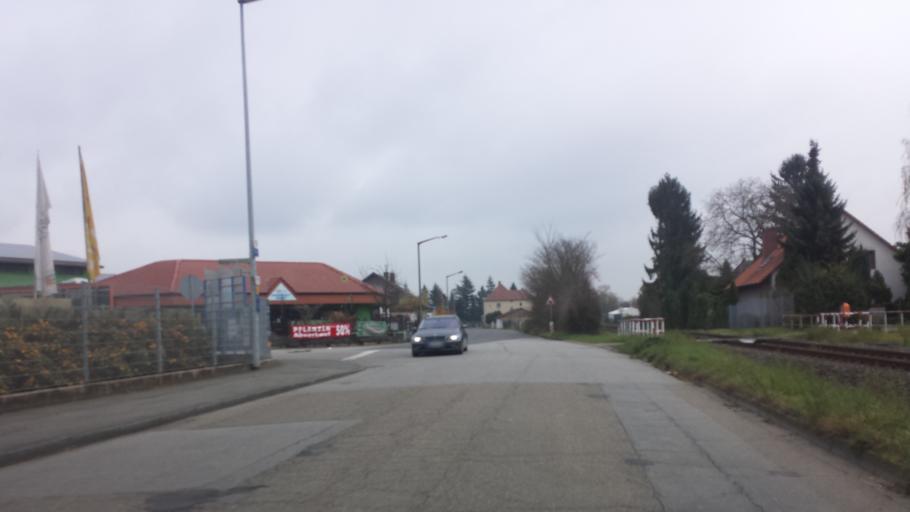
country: DE
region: Hesse
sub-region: Regierungsbezirk Darmstadt
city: Burstadt
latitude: 49.6454
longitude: 8.4660
